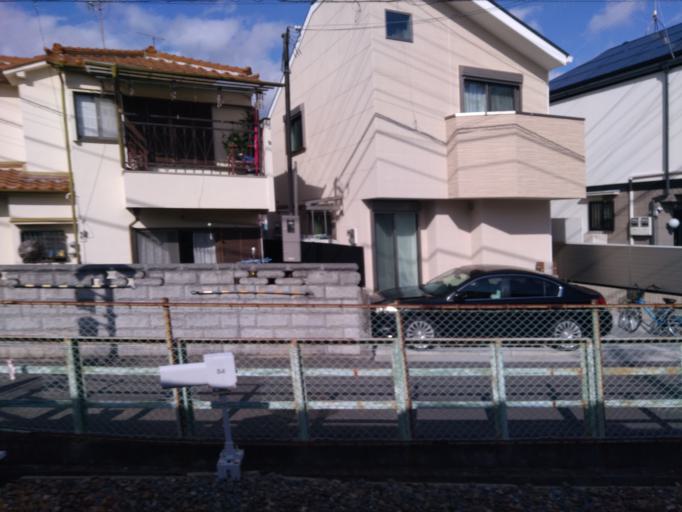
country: JP
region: Hyogo
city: Kawanishi
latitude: 34.8205
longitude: 135.3840
